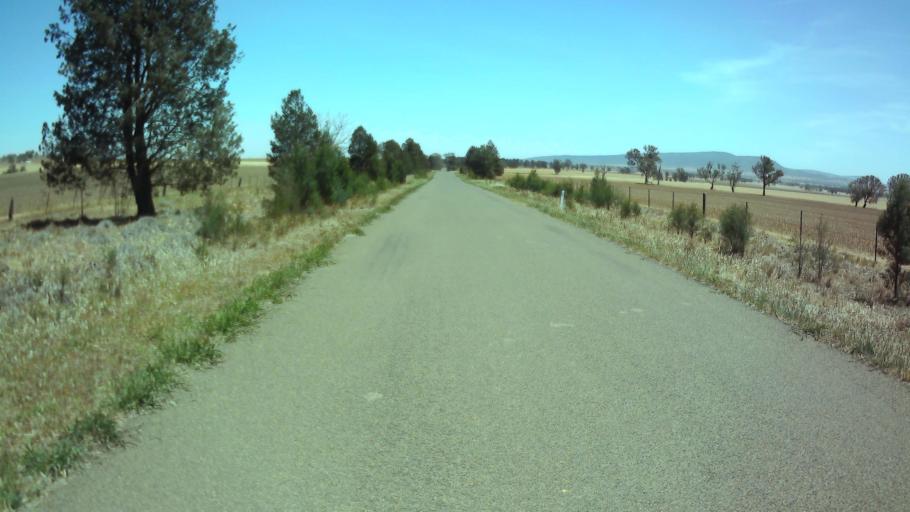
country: AU
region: New South Wales
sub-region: Weddin
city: Grenfell
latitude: -34.0531
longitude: 148.2180
